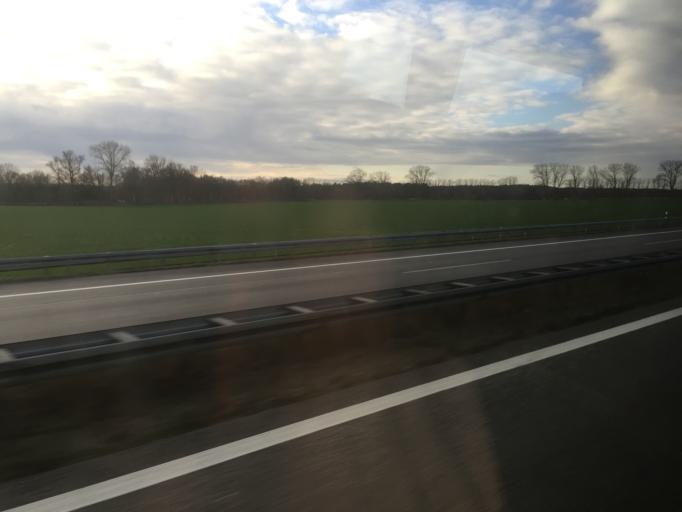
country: DE
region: Mecklenburg-Vorpommern
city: Neustadt-Glewe
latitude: 53.4095
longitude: 11.5647
